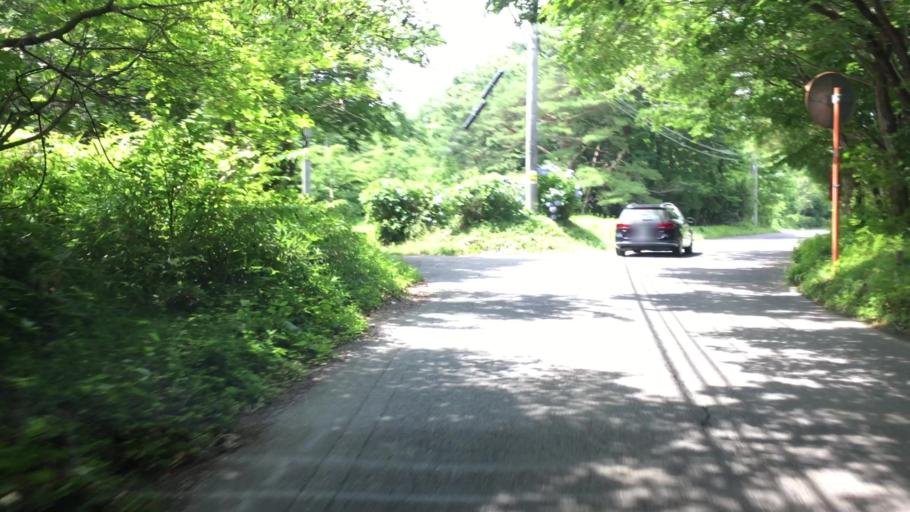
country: JP
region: Tochigi
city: Kuroiso
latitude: 37.0494
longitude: 139.9462
